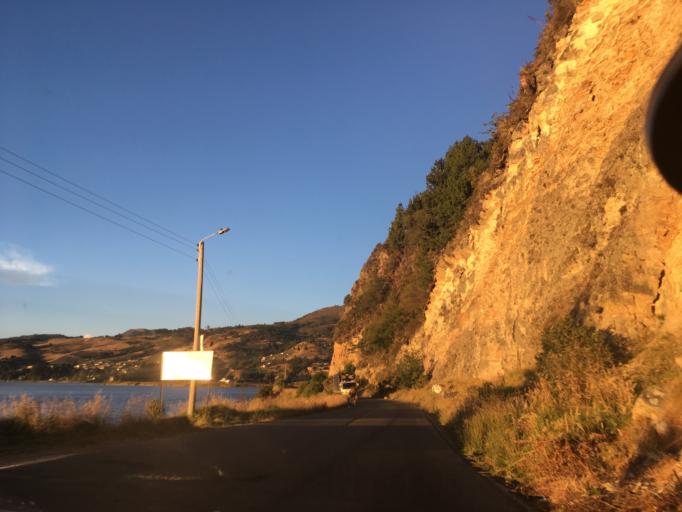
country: CO
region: Boyaca
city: Aquitania
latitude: 5.5499
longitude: -72.8819
